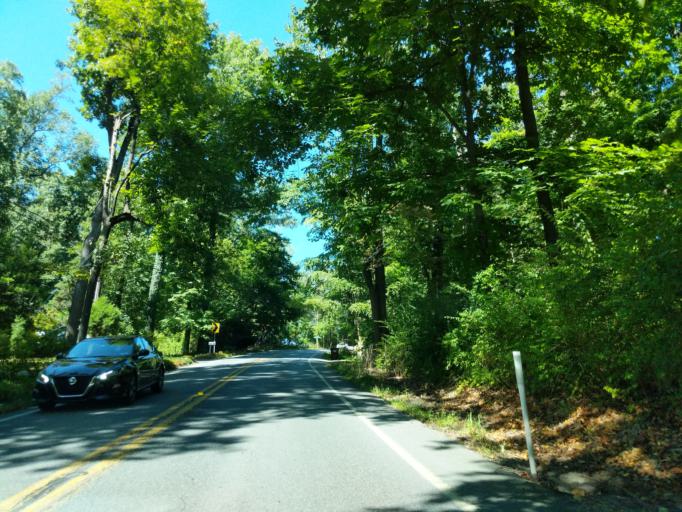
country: US
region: Pennsylvania
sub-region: Montgomery County
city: East Greenville
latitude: 40.4429
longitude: -75.4877
